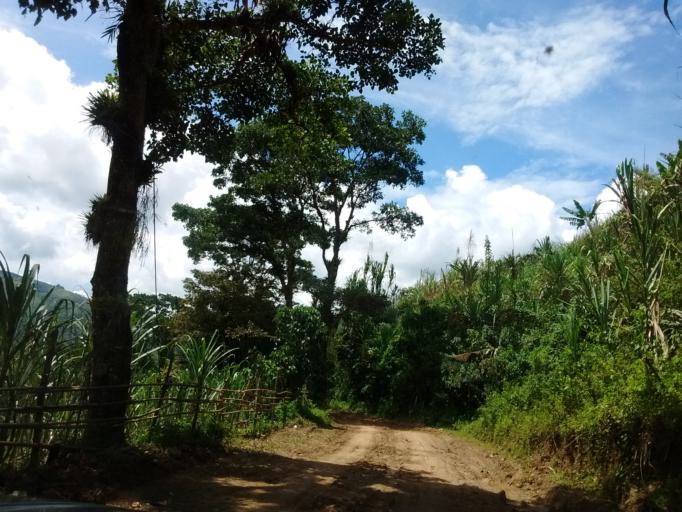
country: CO
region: Cauca
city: Villa Rica
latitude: 2.6622
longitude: -76.7686
